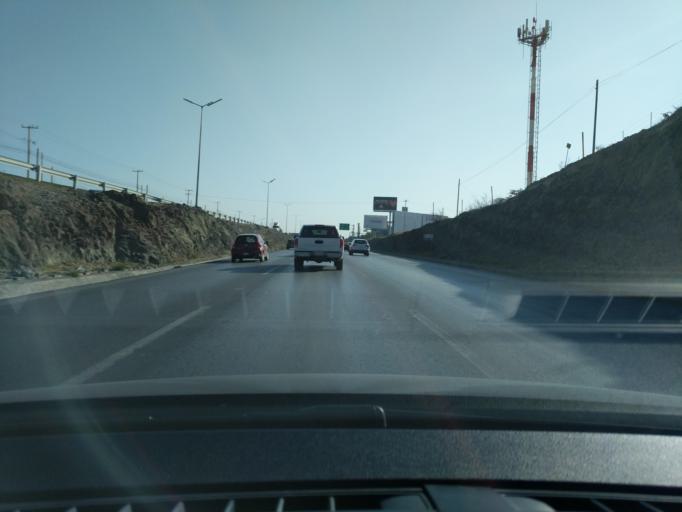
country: MX
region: Coahuila
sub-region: Ramos Arizpe
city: Ramos Arizpe
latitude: 25.5137
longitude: -100.9590
